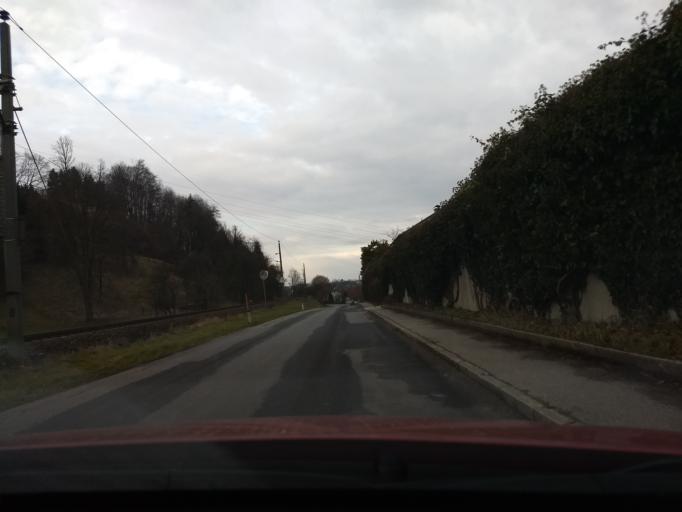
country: AT
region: Upper Austria
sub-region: Politischer Bezirk Steyr-Land
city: Garsten
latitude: 48.0105
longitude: 14.4068
